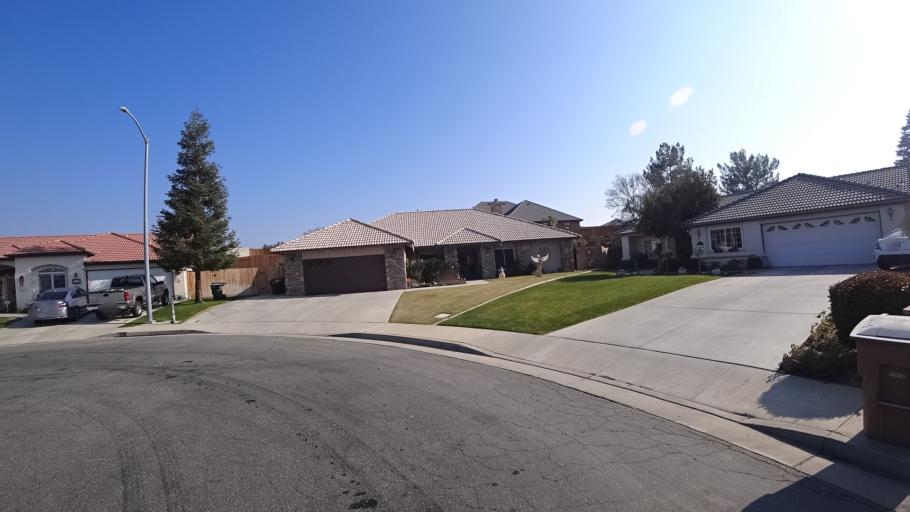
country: US
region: California
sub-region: Kern County
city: Oildale
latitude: 35.4071
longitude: -118.8704
